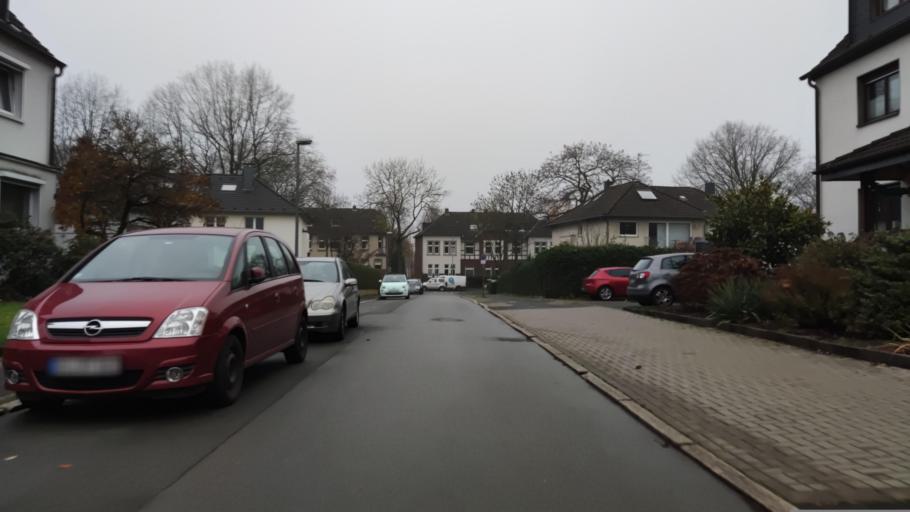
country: DE
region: North Rhine-Westphalia
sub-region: Regierungsbezirk Arnsberg
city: Bochum
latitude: 51.4543
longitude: 7.2359
